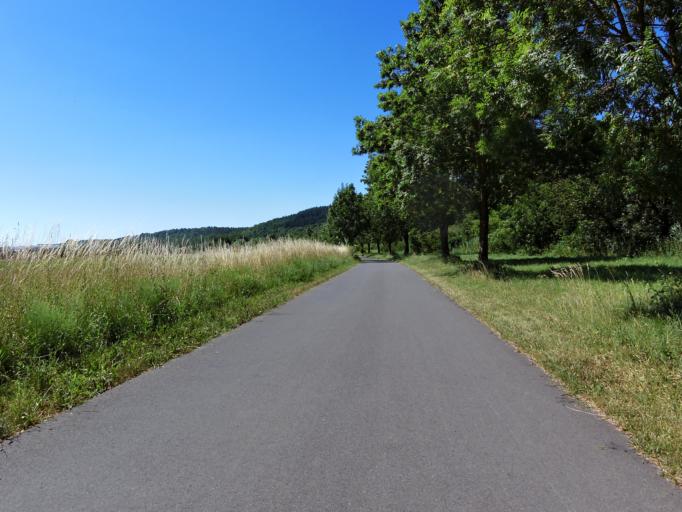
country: DE
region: Bavaria
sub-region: Regierungsbezirk Unterfranken
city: Eibelstadt
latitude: 49.7374
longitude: 9.9873
